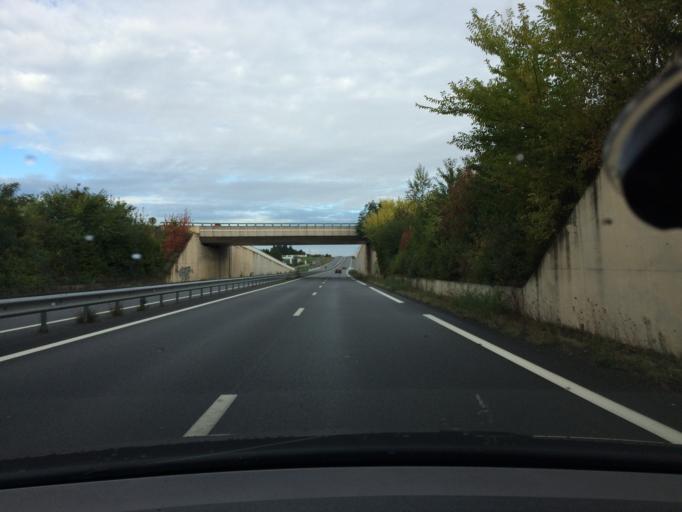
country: FR
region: Brittany
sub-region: Departement d'Ille-et-Vilaine
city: Janze
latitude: 47.9702
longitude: -1.5357
